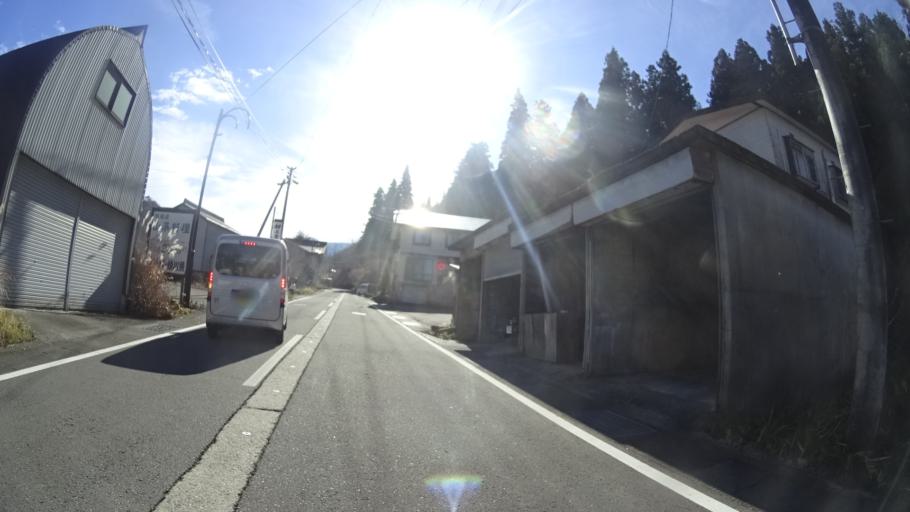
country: JP
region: Niigata
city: Muikamachi
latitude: 37.1925
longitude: 139.0806
